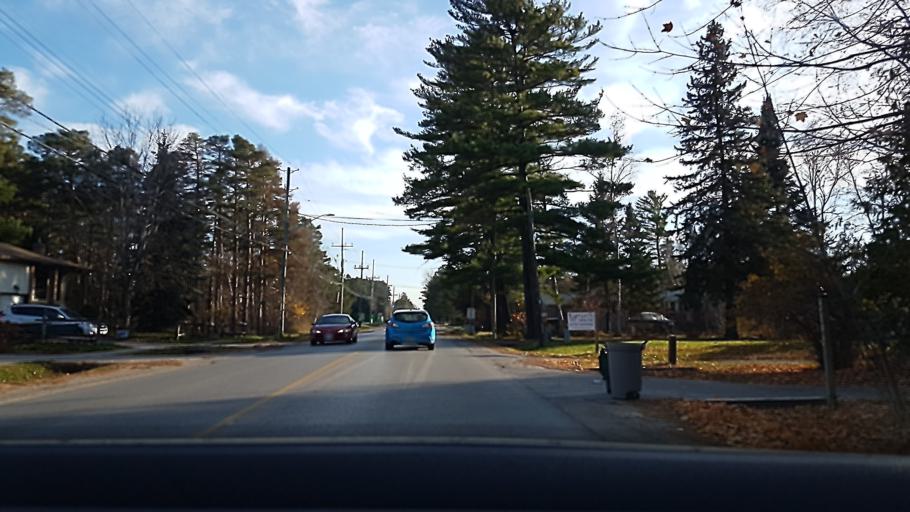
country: CA
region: Ontario
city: Keswick
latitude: 44.3206
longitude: -79.5410
